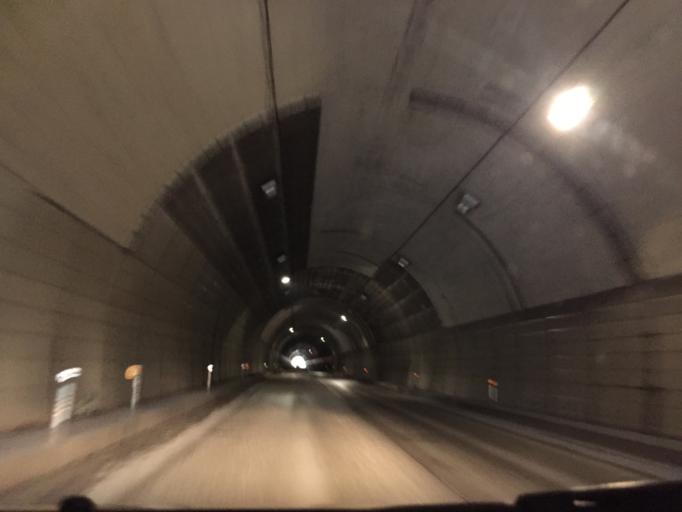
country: JP
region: Tochigi
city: Kuroiso
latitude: 37.0694
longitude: 139.7473
